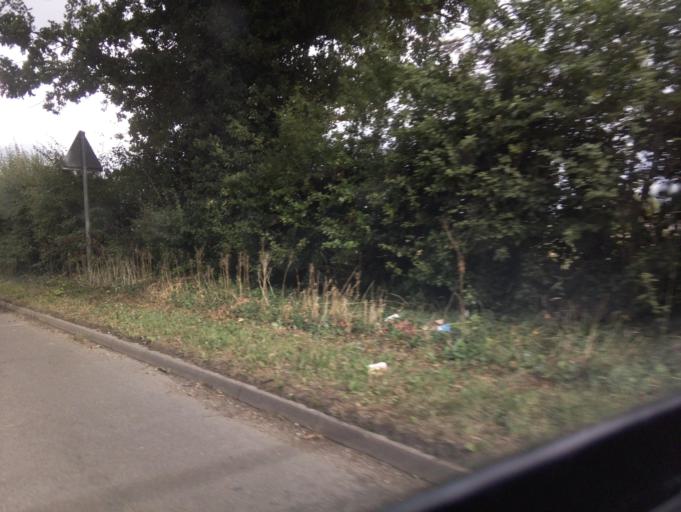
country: GB
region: England
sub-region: Staffordshire
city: Eccleshall
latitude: 52.8731
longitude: -2.2465
